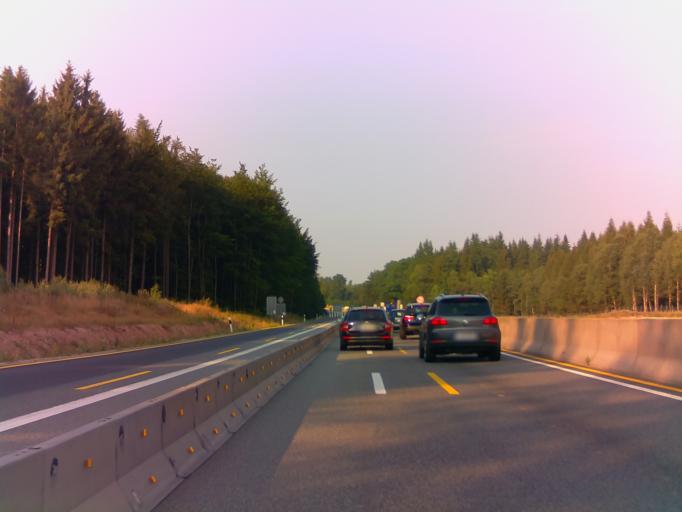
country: DE
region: Hesse
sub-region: Regierungsbezirk Kassel
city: Friedewald
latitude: 50.9006
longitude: 9.8690
